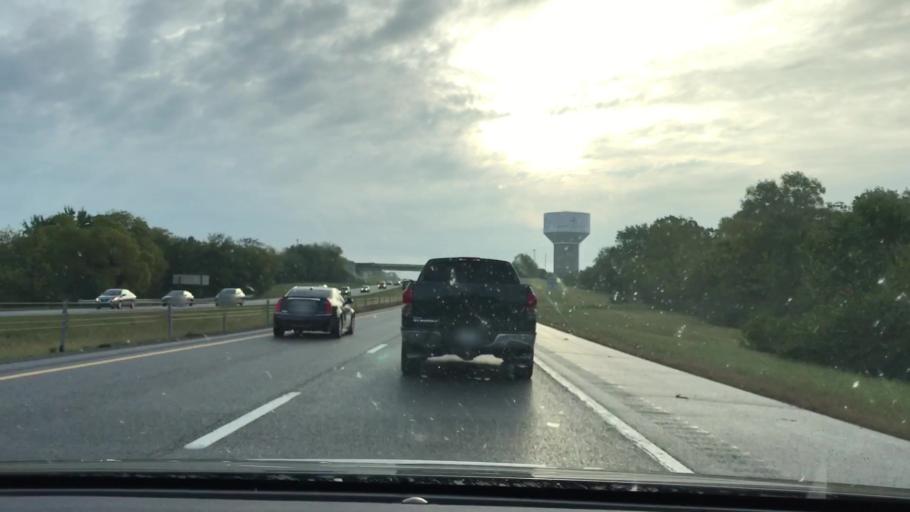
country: US
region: Tennessee
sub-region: Sumner County
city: Hendersonville
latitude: 36.3315
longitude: -86.5828
